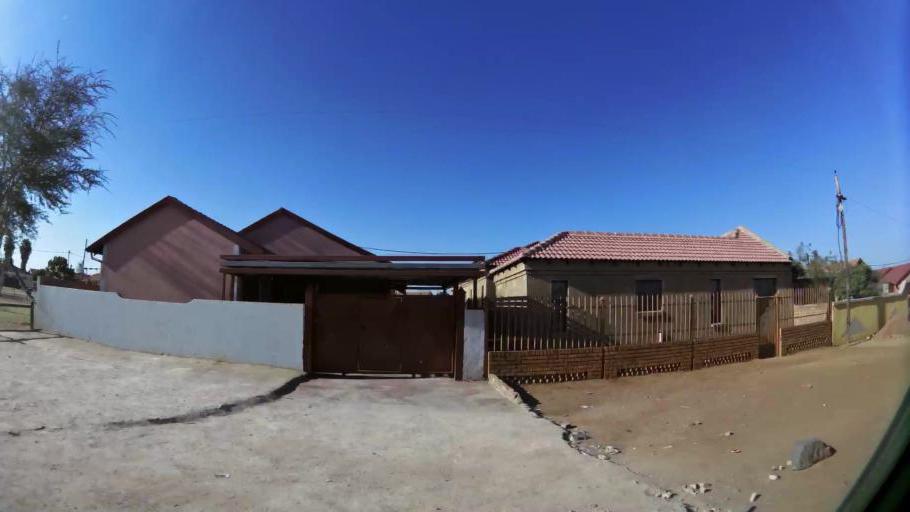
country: ZA
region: Gauteng
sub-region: City of Tshwane Metropolitan Municipality
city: Mabopane
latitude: -25.5860
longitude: 28.1068
